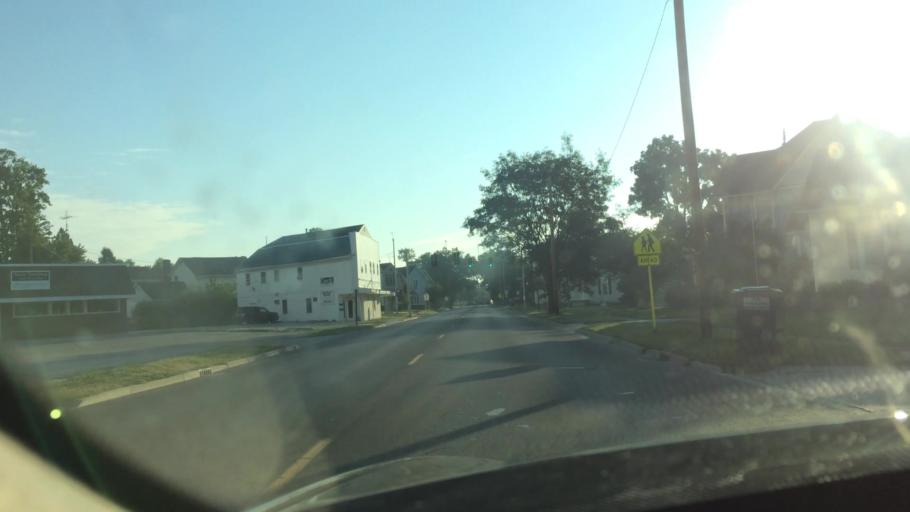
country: US
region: Ohio
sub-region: Hancock County
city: Findlay
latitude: 41.0309
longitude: -83.6546
